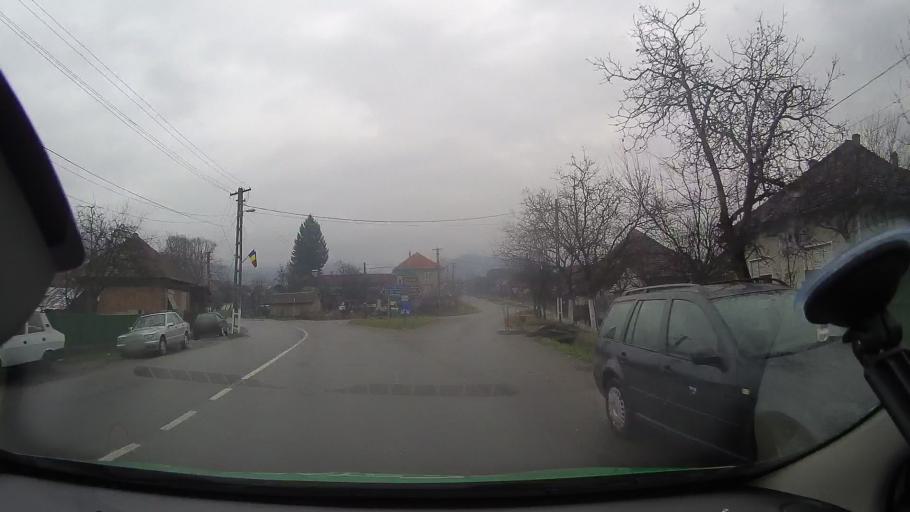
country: RO
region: Arad
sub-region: Comuna Gurahont
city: Gurahont
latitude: 46.2737
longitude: 22.3353
